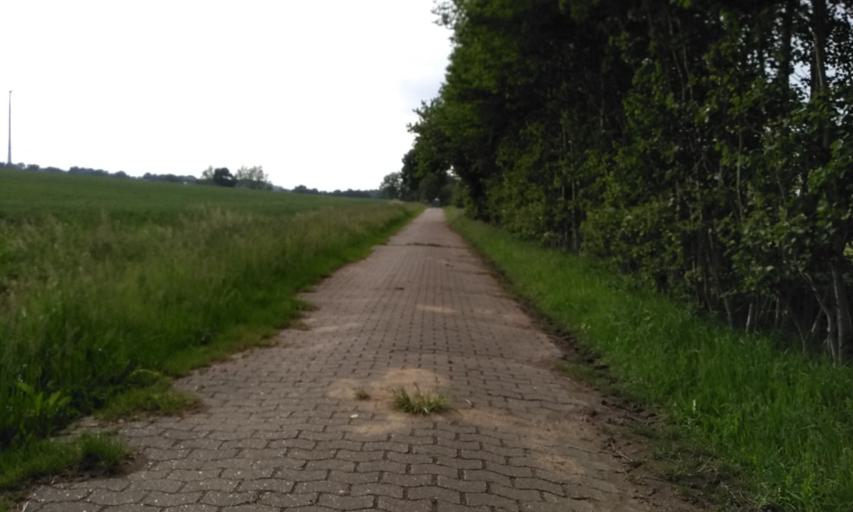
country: DE
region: Lower Saxony
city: Nottensdorf
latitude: 53.4649
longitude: 9.6277
